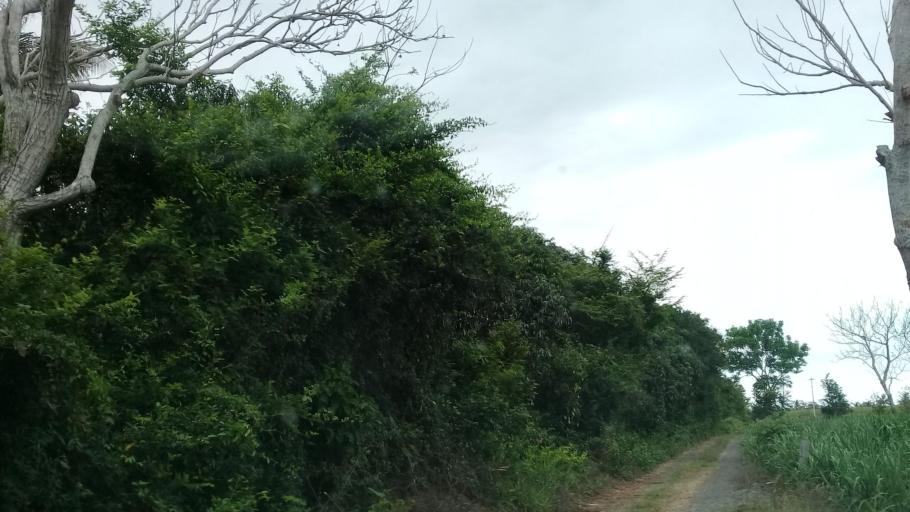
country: MX
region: Veracruz
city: Ursulo Galvan
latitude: 19.3837
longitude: -96.3621
